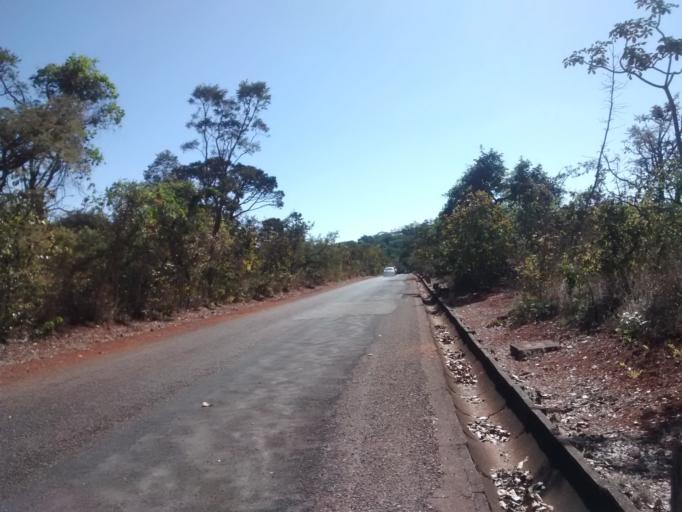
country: BR
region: Federal District
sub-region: Brasilia
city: Brasilia
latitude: -15.7409
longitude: -47.9236
